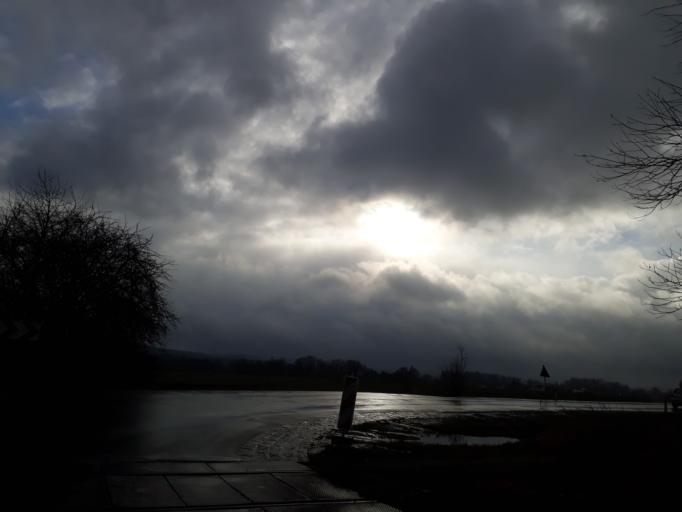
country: DE
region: Saxony
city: Herrnhut
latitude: 51.0084
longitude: 14.7285
